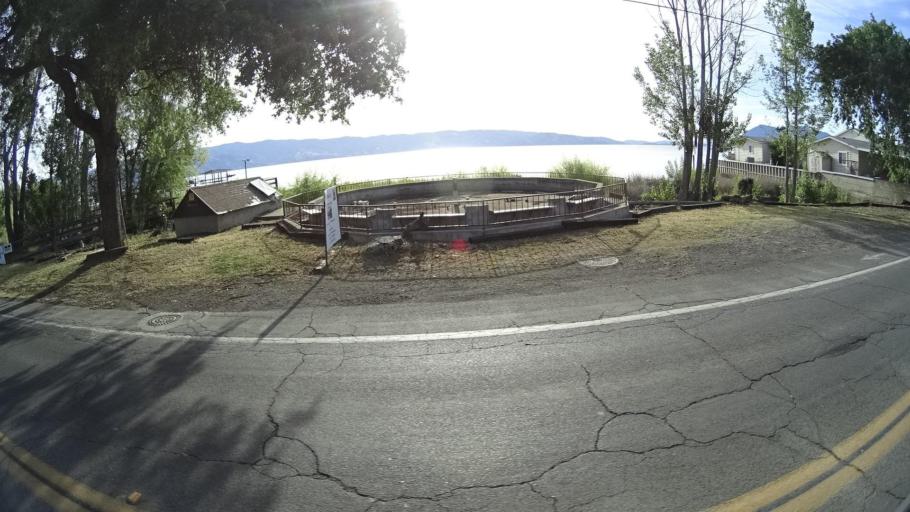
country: US
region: California
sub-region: Lake County
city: Lakeport
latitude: 39.0636
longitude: -122.9139
